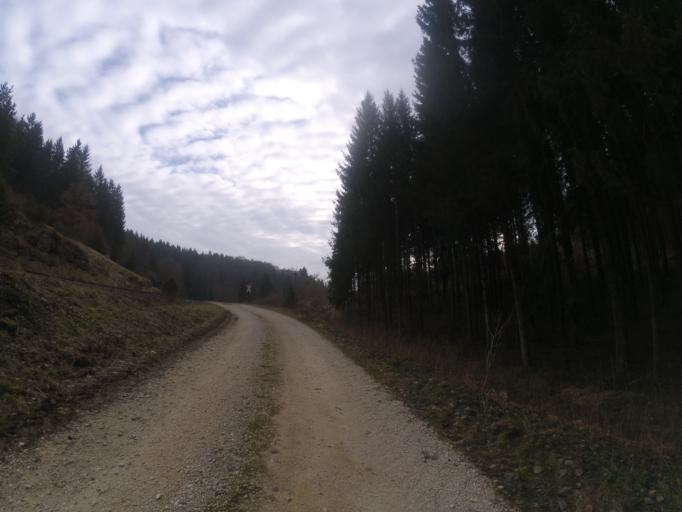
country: DE
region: Baden-Wuerttemberg
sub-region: Tuebingen Region
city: Mehrstetten
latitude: 48.3606
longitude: 9.5420
